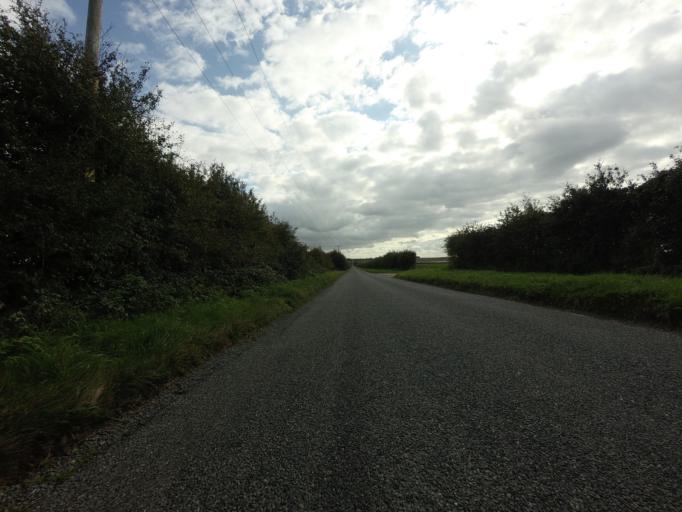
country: GB
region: England
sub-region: Norfolk
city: Heacham
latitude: 52.9145
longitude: 0.5428
